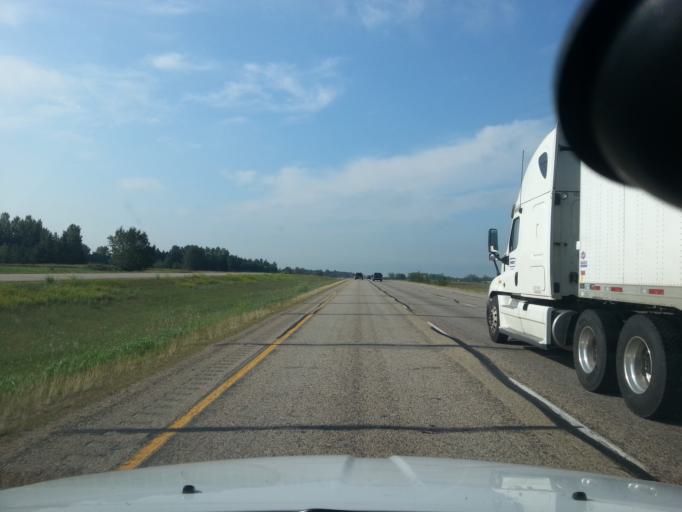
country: CA
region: Alberta
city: Lacombe
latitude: 52.5354
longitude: -113.6720
